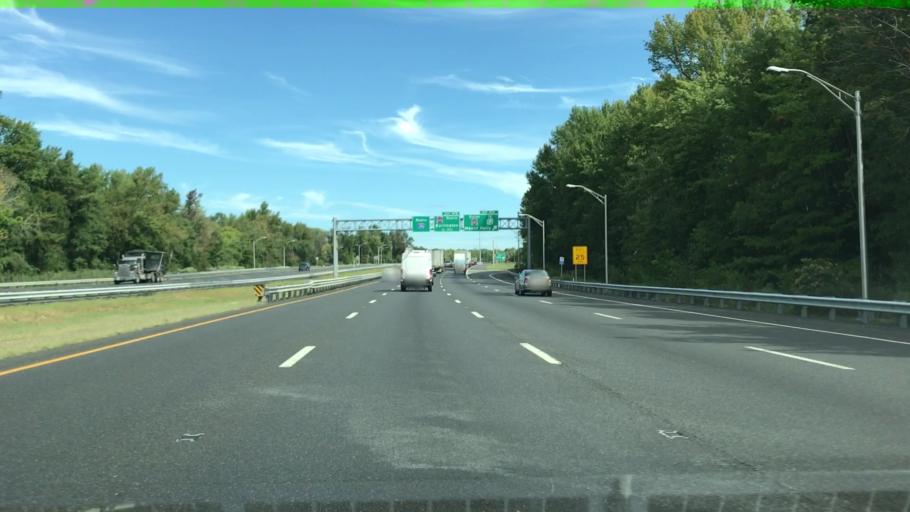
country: US
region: New Jersey
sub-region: Burlington County
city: Willingboro
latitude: 40.0409
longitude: -74.8369
